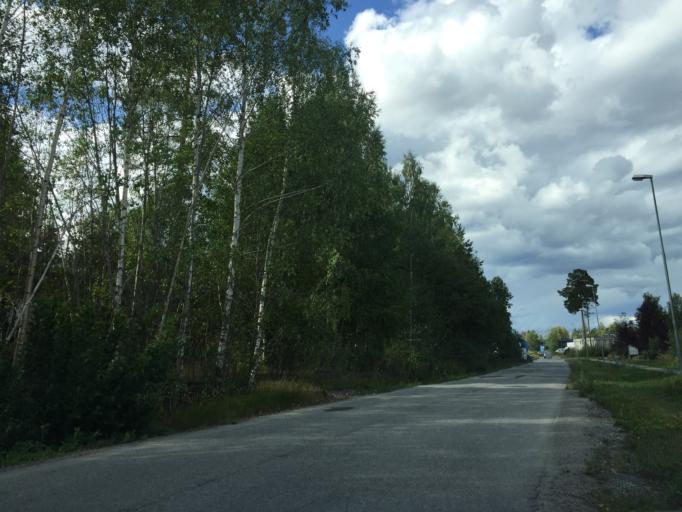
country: NO
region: Ostfold
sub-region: Askim
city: Askim
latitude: 59.5916
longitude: 11.1303
